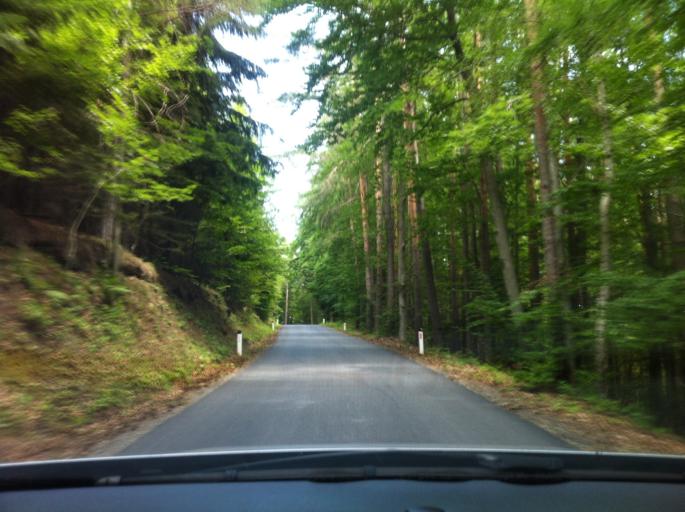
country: AT
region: Styria
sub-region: Politischer Bezirk Hartberg-Fuerstenfeld
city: Siegersdorf bei Herberstein
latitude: 47.2206
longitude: 15.7639
